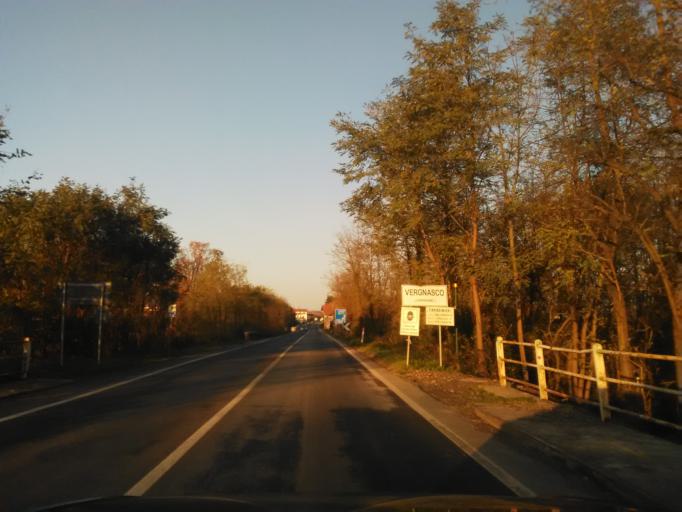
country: IT
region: Piedmont
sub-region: Provincia di Biella
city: Cerrione
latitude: 45.4787
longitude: 8.0721
